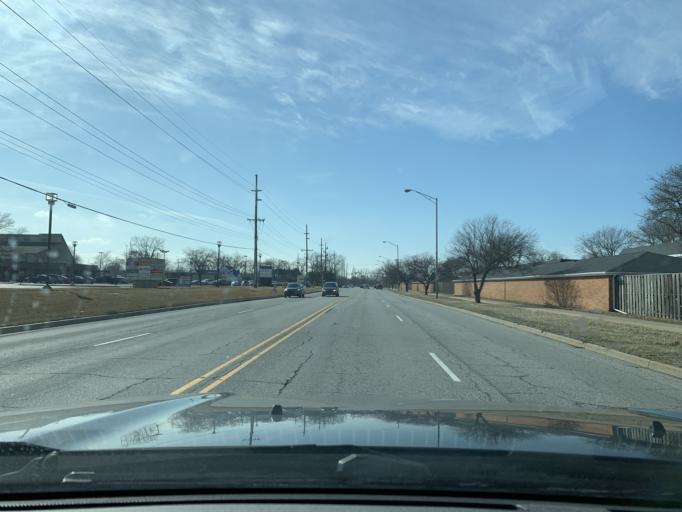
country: US
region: Indiana
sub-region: Lake County
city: Munster
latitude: 41.5377
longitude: -87.4874
